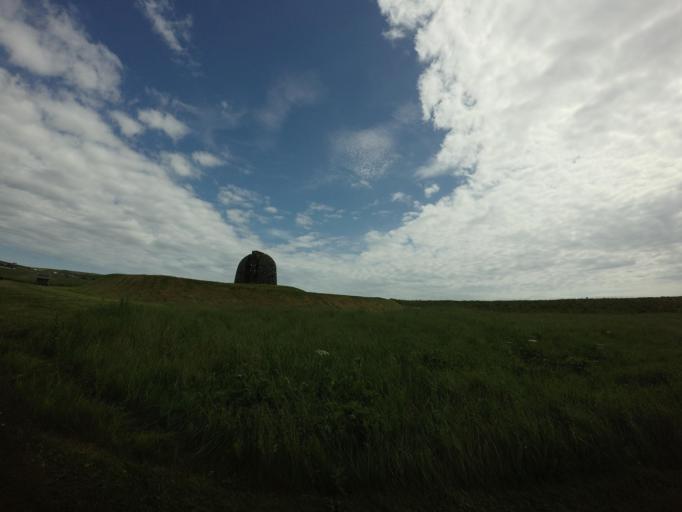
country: GB
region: Scotland
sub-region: Eilean Siar
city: Isle of Lewis
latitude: 58.2869
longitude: -6.2843
